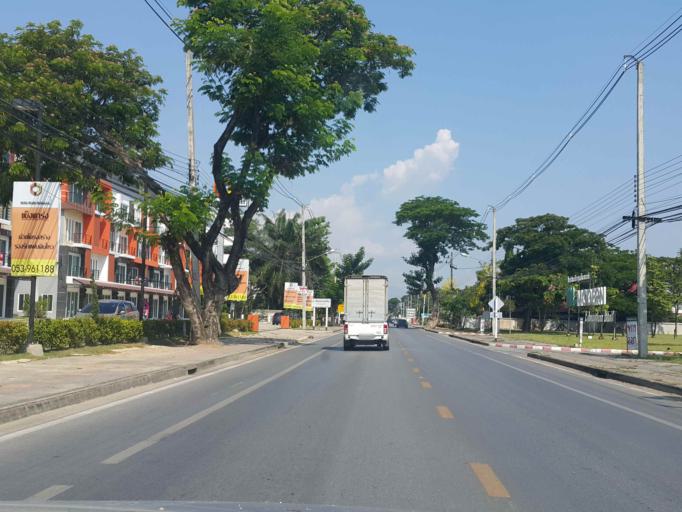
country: TH
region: Chiang Mai
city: San Kamphaeng
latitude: 18.7731
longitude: 99.0643
